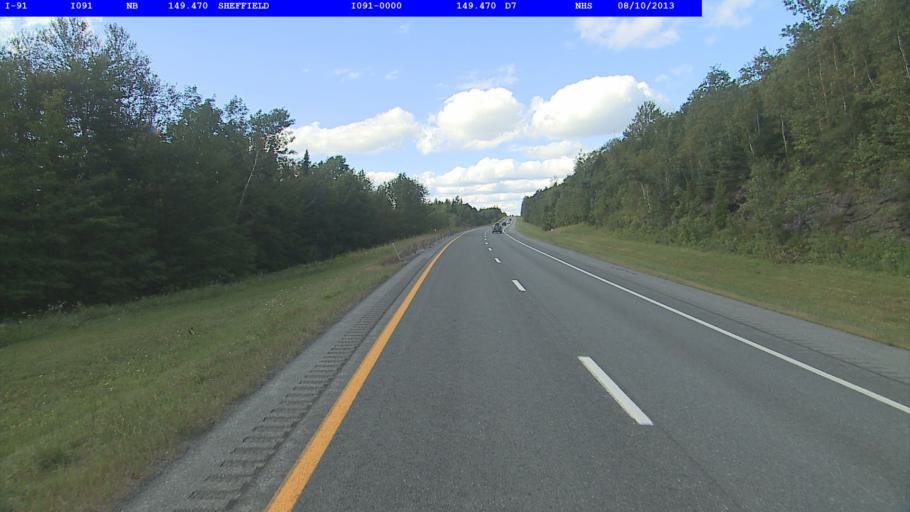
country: US
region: Vermont
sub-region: Caledonia County
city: Lyndonville
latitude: 44.6569
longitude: -72.1338
